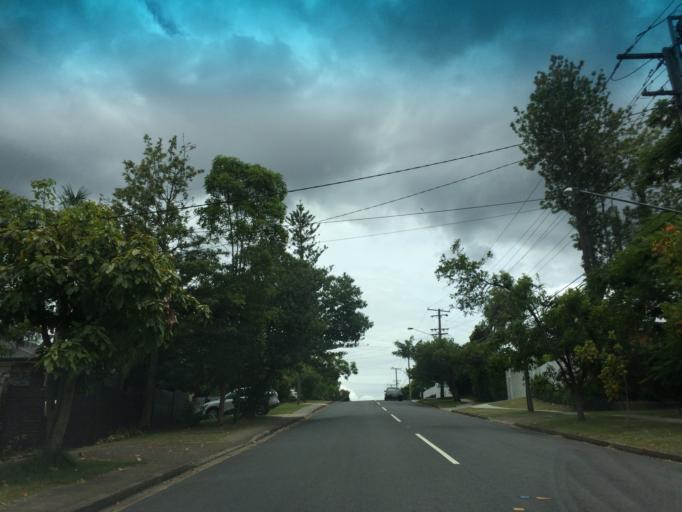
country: AU
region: Queensland
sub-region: Brisbane
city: Kenmore Hills
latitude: -27.5159
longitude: 152.9464
